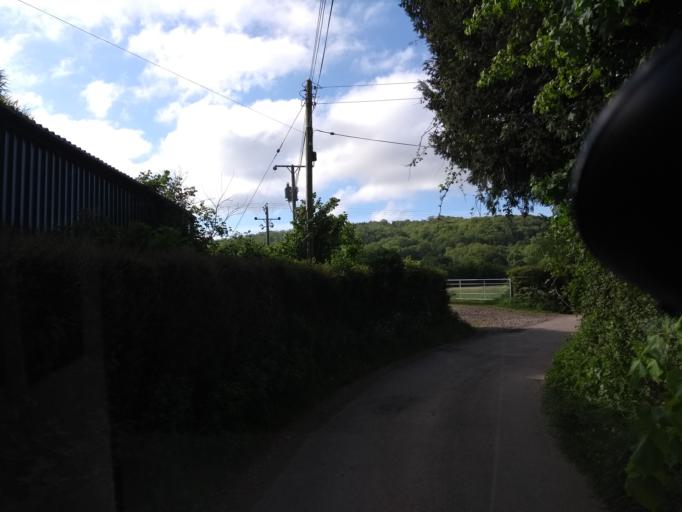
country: GB
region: England
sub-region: Somerset
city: Taunton
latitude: 50.9660
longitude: -3.1105
